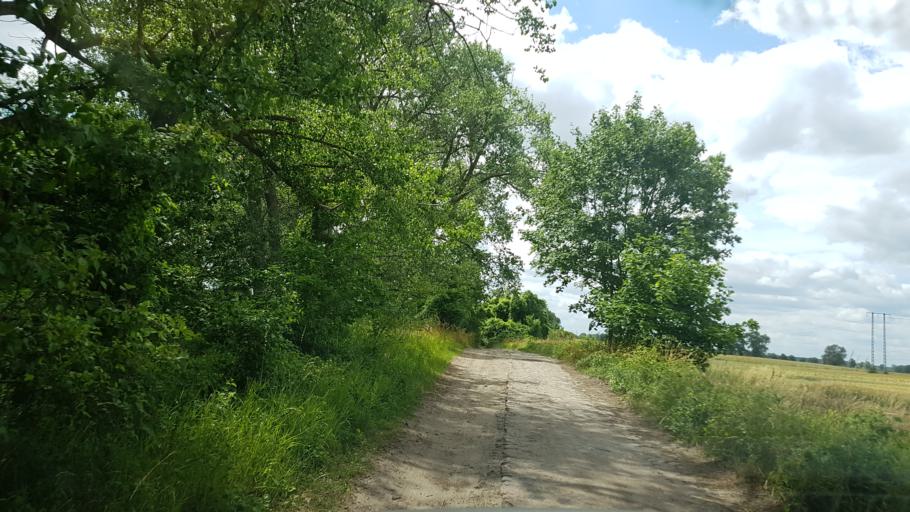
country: PL
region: West Pomeranian Voivodeship
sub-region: Powiat pyrzycki
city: Lipiany
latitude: 52.9649
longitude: 14.9887
